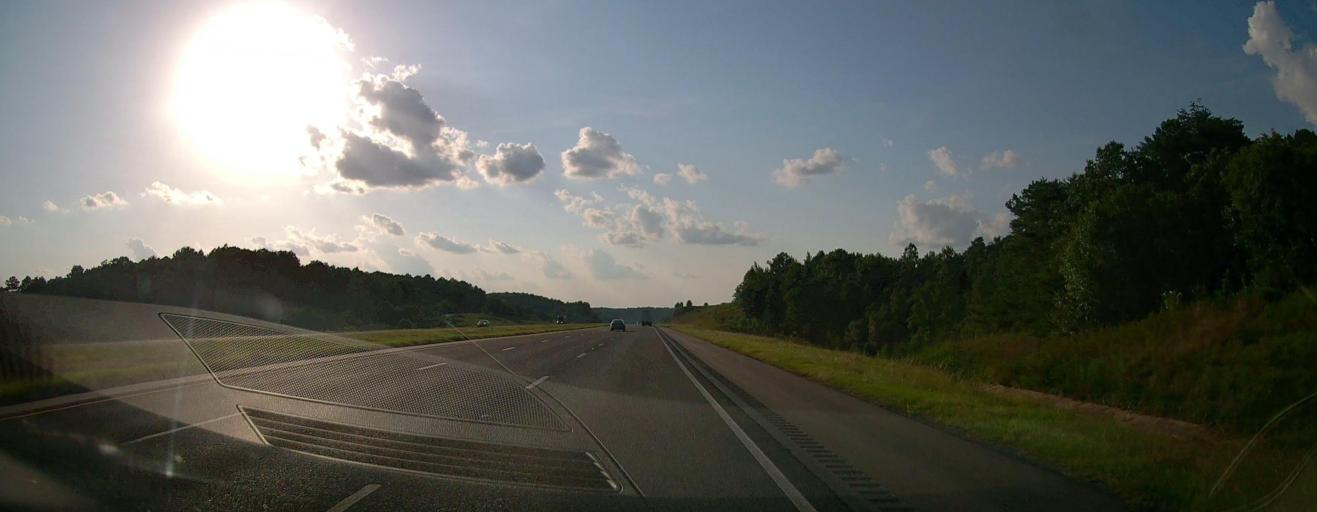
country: US
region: Alabama
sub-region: Walker County
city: Dora
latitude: 33.6978
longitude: -87.1306
